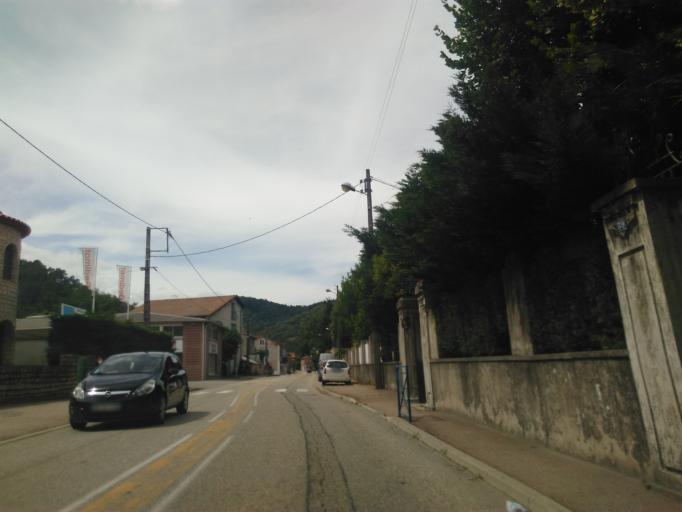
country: FR
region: Rhone-Alpes
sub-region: Departement de l'Ardeche
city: Labegude
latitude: 44.6538
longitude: 4.3194
